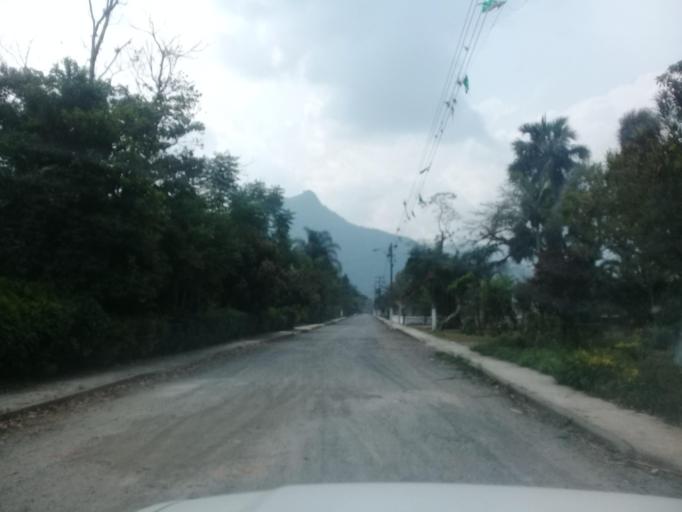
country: MX
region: Veracruz
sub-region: Ixtaczoquitlan
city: Capoluca
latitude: 18.8199
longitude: -96.9931
